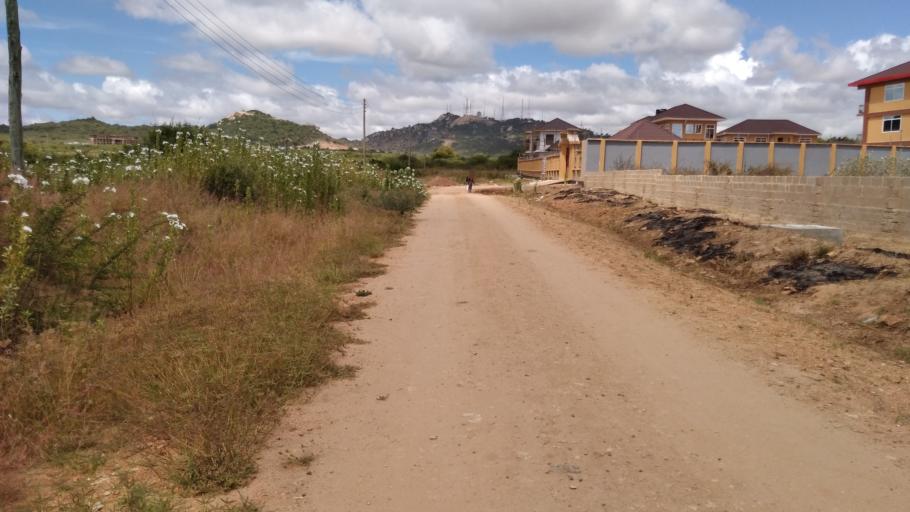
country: TZ
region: Dodoma
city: Dodoma
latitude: -6.1896
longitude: 35.7571
